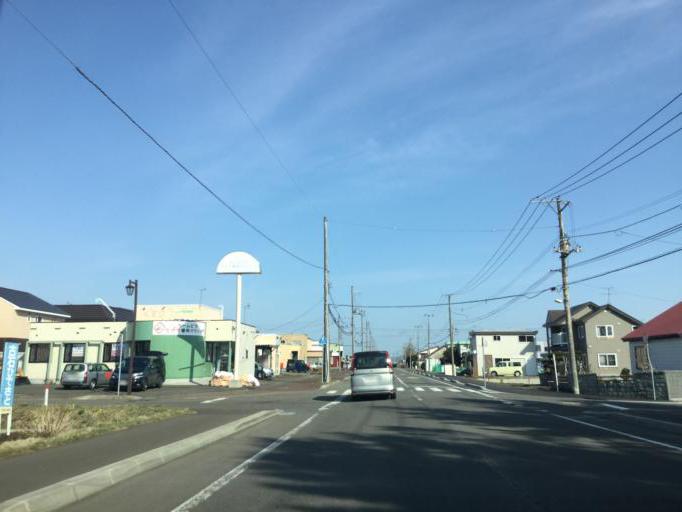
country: JP
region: Hokkaido
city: Ebetsu
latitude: 43.1490
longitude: 141.6501
